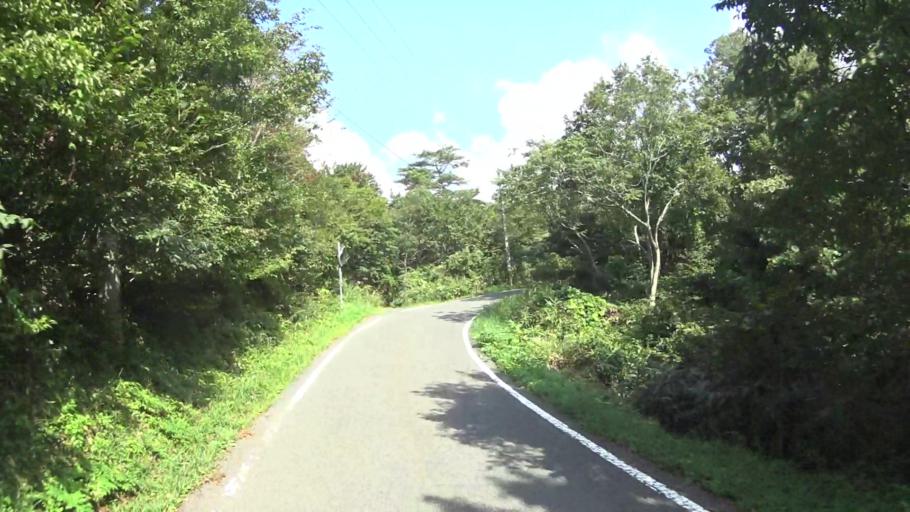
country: JP
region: Kyoto
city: Miyazu
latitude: 35.6473
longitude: 135.1800
